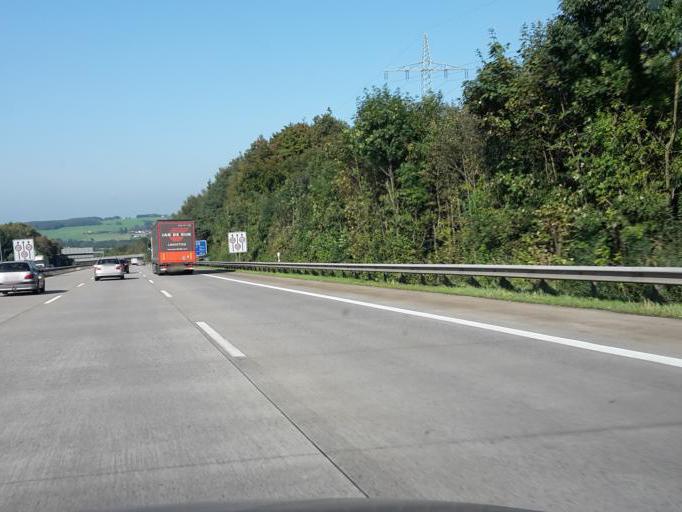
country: DE
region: Rheinland-Pfalz
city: Breitscheid
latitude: 50.6060
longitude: 7.4291
